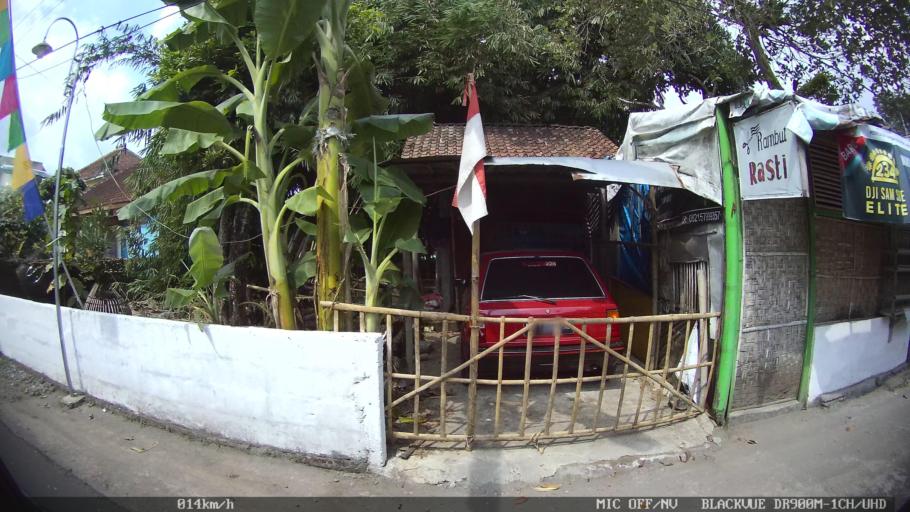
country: ID
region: Daerah Istimewa Yogyakarta
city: Gamping Lor
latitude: -7.8082
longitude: 110.3370
